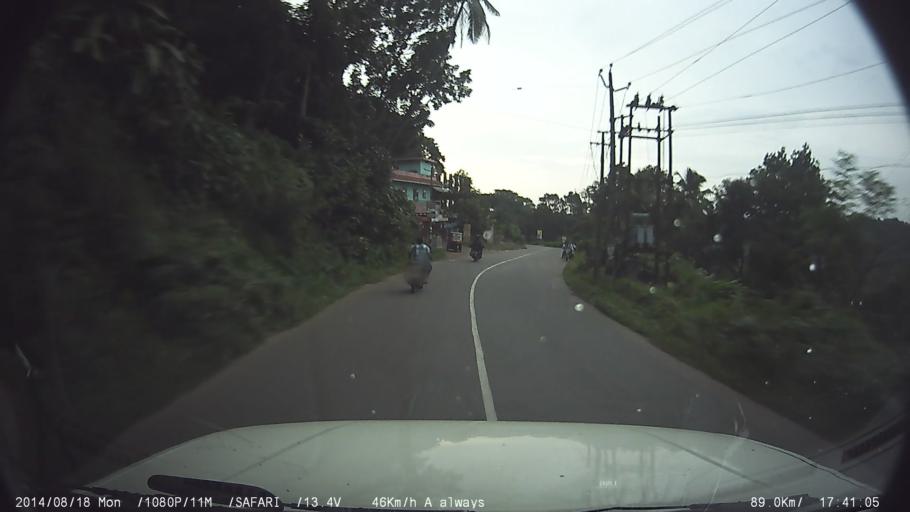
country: IN
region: Kerala
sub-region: Ernakulam
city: Muvattupuzha
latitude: 9.9268
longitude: 76.5799
